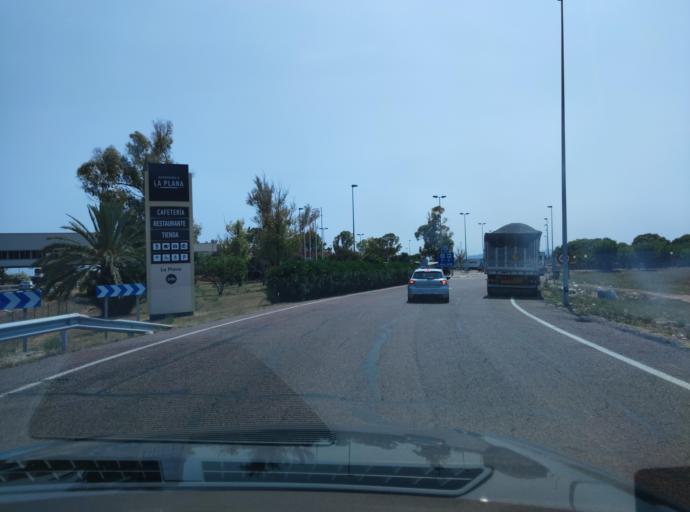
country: ES
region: Valencia
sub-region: Provincia de Castello
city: Alquerias del Nino Perdido
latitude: 39.8662
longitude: -0.1226
